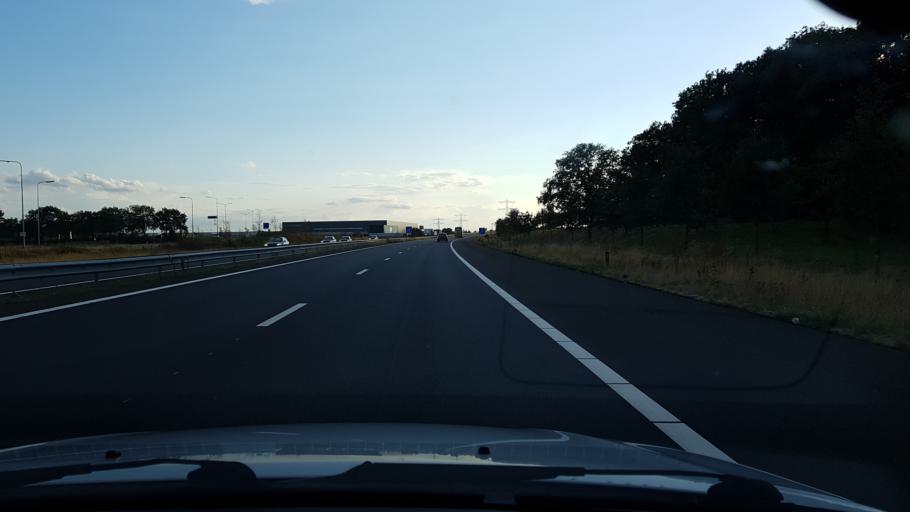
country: NL
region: Limburg
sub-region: Gemeente Maasgouw
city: Maasbracht
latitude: 51.1296
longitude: 5.9009
